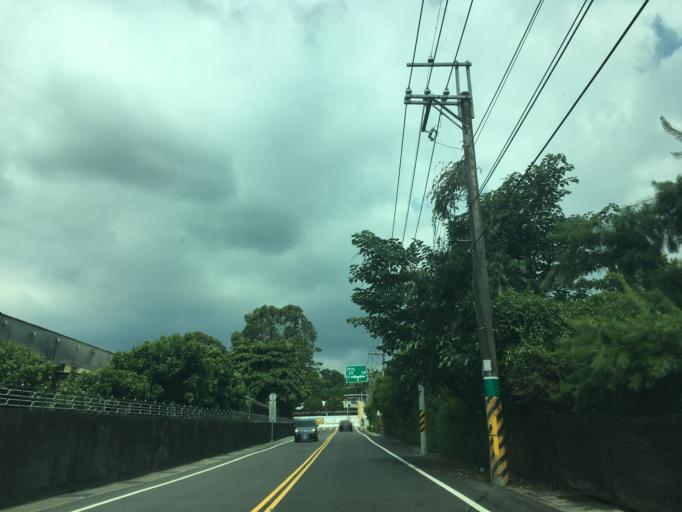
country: TW
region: Taiwan
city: Fengyuan
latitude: 24.2297
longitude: 120.8021
